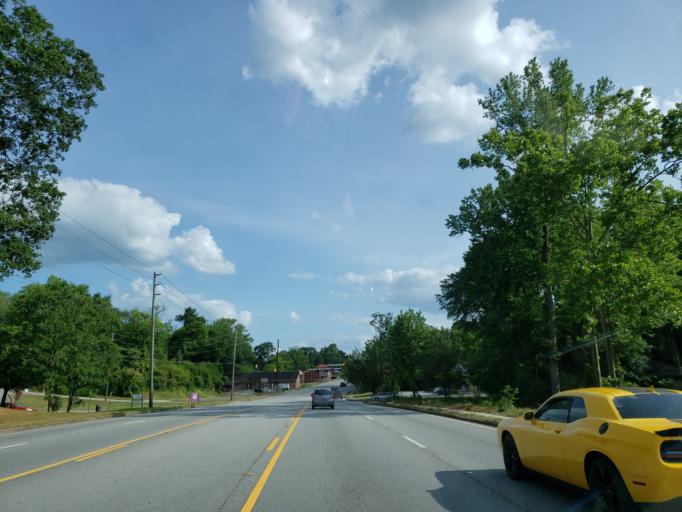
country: US
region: Georgia
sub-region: Carroll County
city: Carrollton
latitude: 33.5858
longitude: -85.0784
